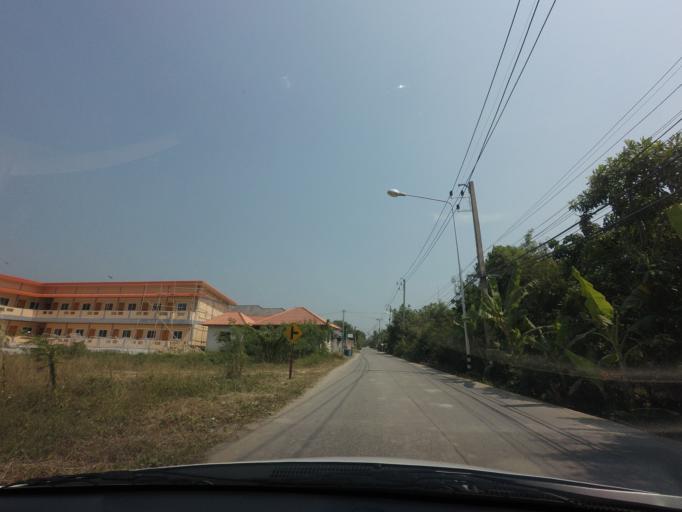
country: TH
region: Nakhon Pathom
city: Sam Phran
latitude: 13.7483
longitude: 100.2627
